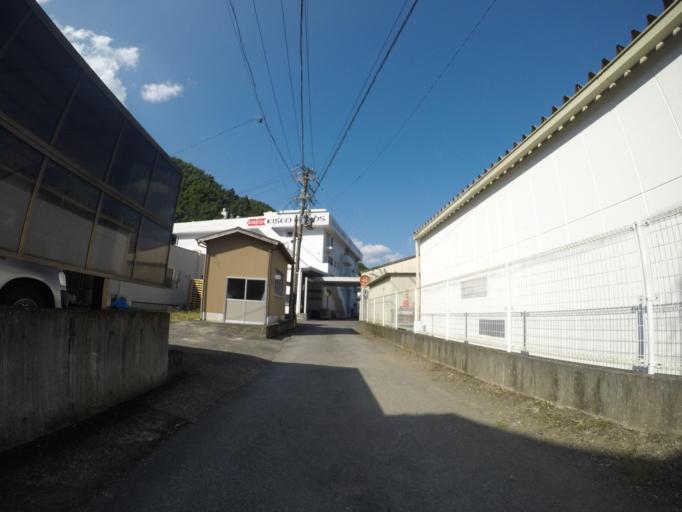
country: JP
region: Shizuoka
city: Shizuoka-shi
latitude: 35.1073
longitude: 138.4646
